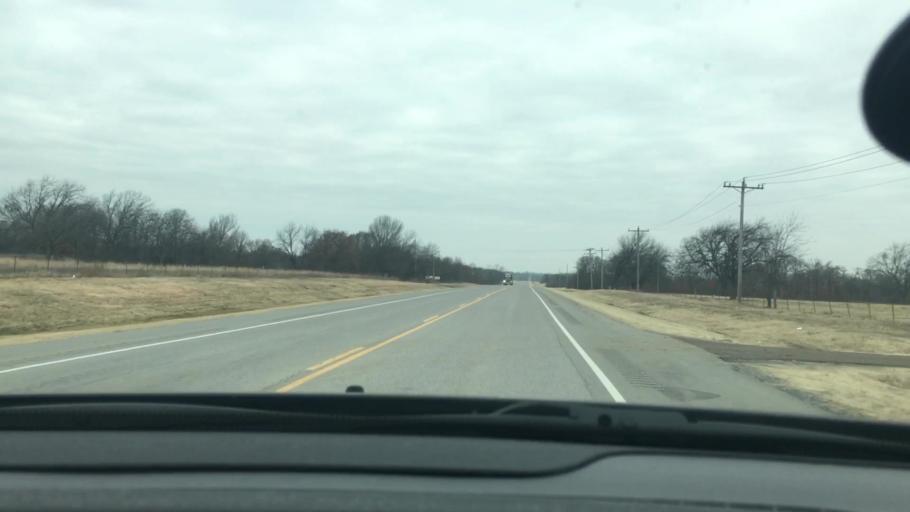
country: US
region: Oklahoma
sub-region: Carter County
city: Healdton
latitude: 34.4924
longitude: -97.4238
